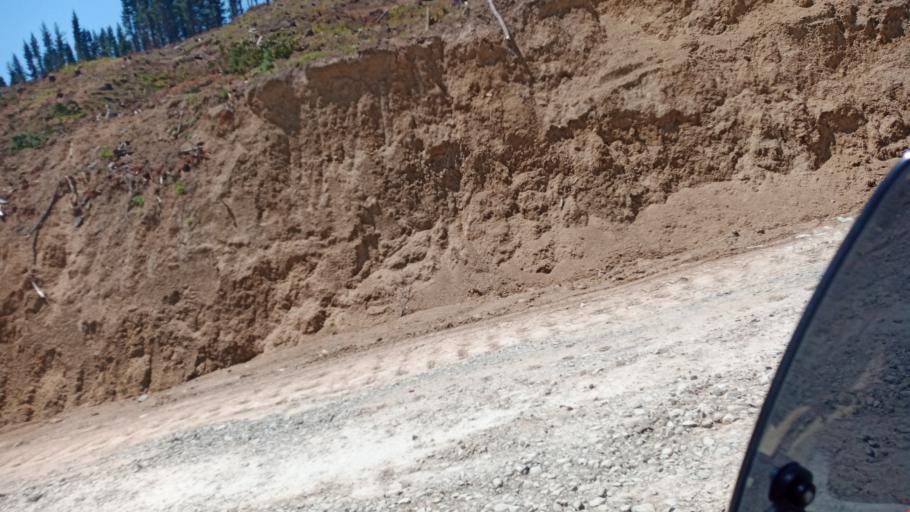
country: NZ
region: Gisborne
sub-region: Gisborne District
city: Gisborne
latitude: -38.2769
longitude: 177.9992
